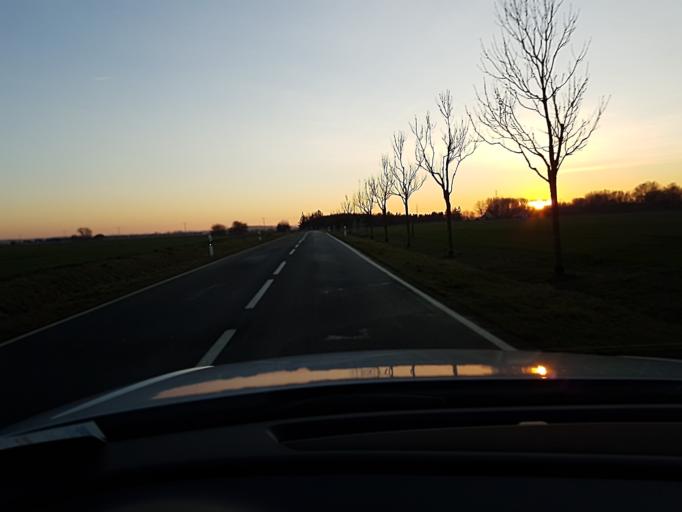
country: DE
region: Mecklenburg-Vorpommern
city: Wiek
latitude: 54.5728
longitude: 13.2650
